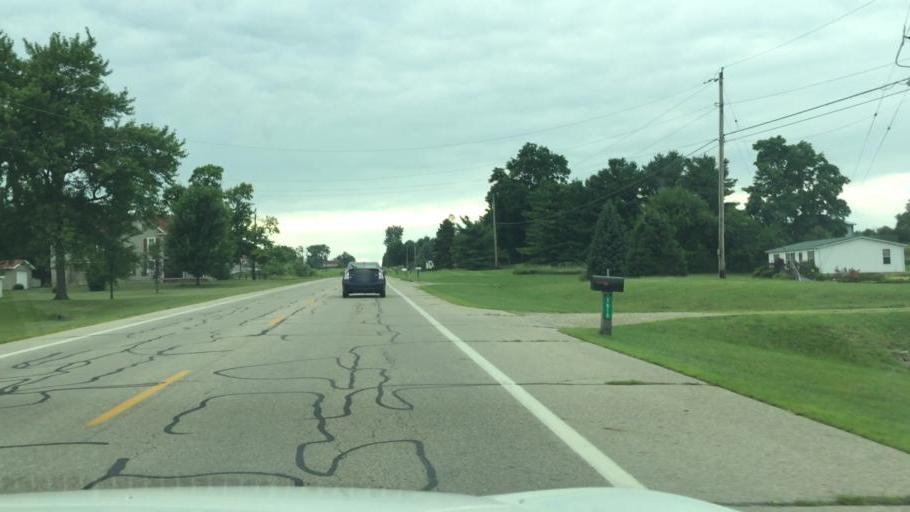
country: US
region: Ohio
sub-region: Champaign County
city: Mechanicsburg
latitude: 40.0784
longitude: -83.5984
